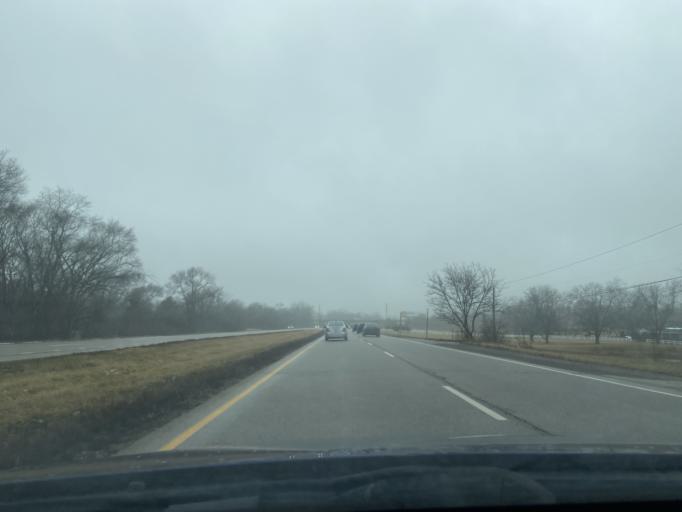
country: US
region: Illinois
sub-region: Lake County
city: Wauconda
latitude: 42.2498
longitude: -88.1406
